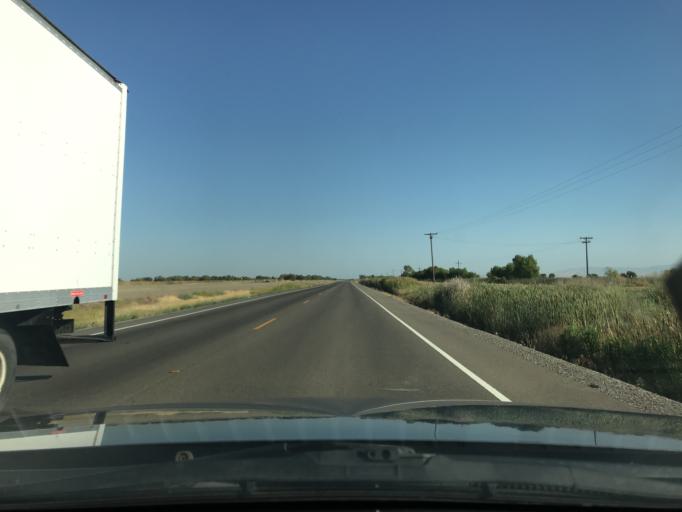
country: US
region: California
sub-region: Merced County
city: Los Banos
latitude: 37.1792
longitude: -120.8338
